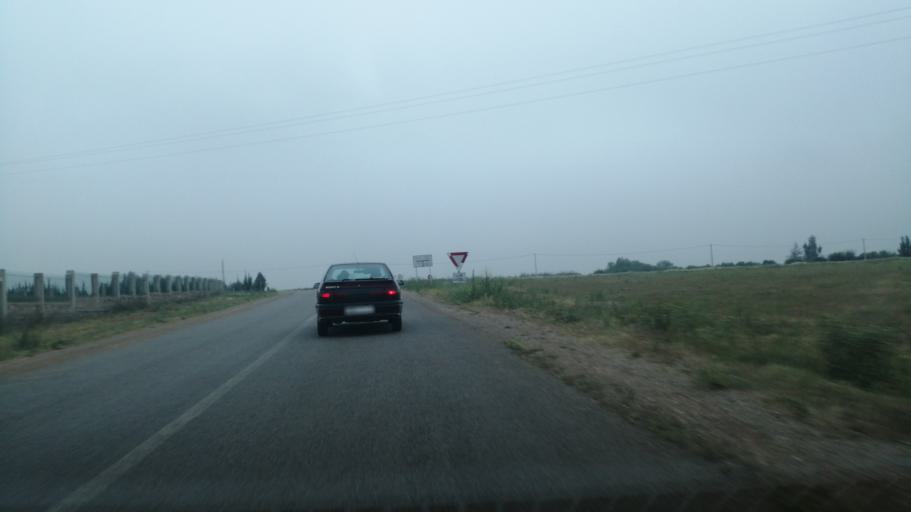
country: MA
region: Rabat-Sale-Zemmour-Zaer
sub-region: Khemisset
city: Tiflet
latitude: 33.7378
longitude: -6.2702
